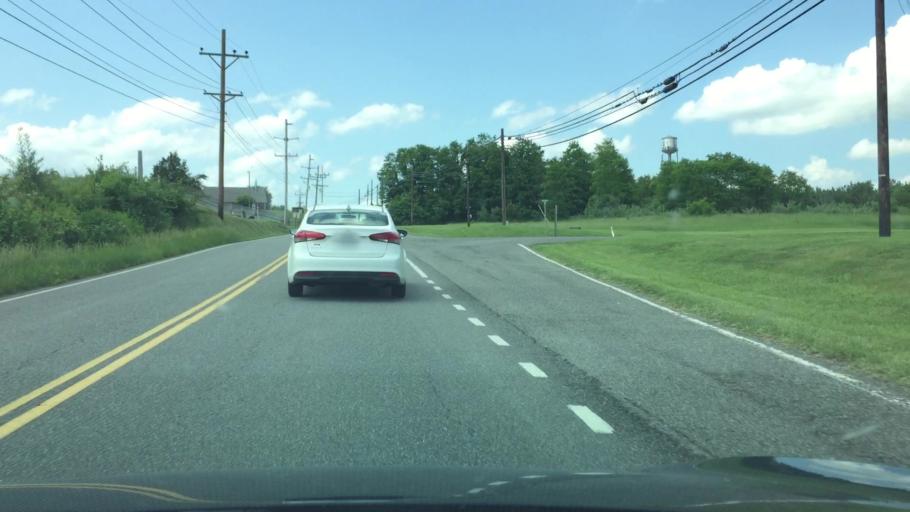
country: US
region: Virginia
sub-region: Pulaski County
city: Dublin
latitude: 37.0837
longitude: -80.6832
